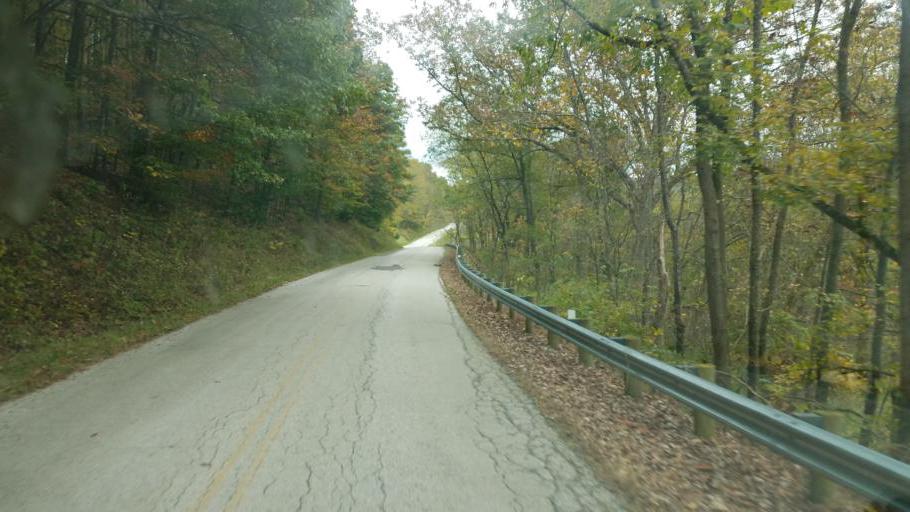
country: US
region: Ohio
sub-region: Ashland County
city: Loudonville
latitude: 40.5540
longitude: -82.1474
